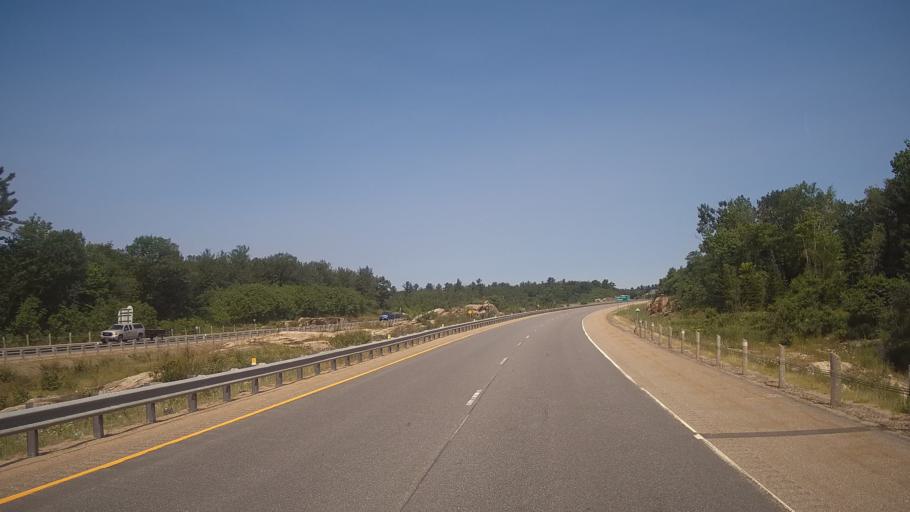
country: CA
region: Ontario
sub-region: Parry Sound District
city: Parry Sound
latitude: 45.1901
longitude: -79.8110
